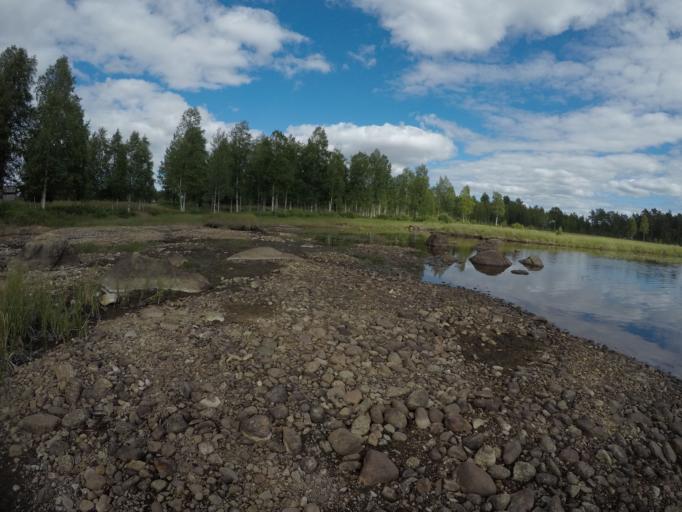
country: SE
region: OErebro
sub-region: Hallefors Kommun
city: Haellefors
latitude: 60.0472
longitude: 14.5013
